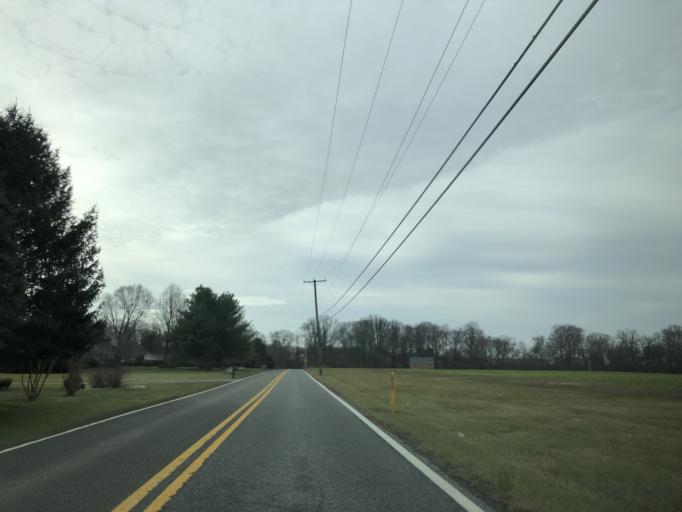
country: US
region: Delaware
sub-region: New Castle County
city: Middletown
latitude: 39.4962
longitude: -75.6880
